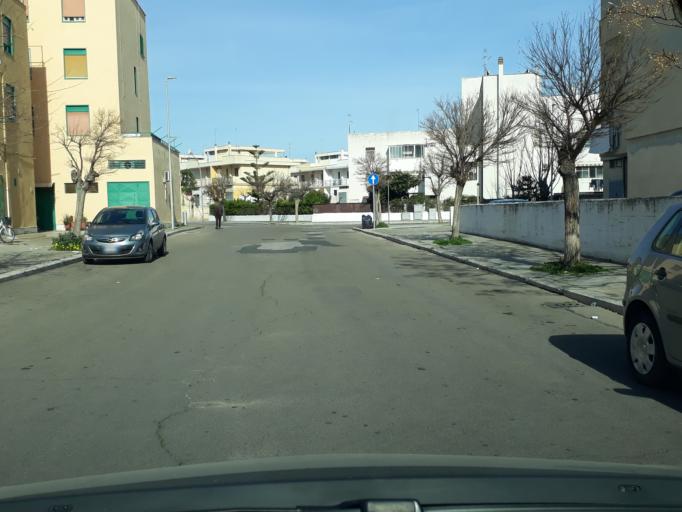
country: IT
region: Apulia
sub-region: Provincia di Brindisi
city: Fasano
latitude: 40.8295
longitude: 17.3628
